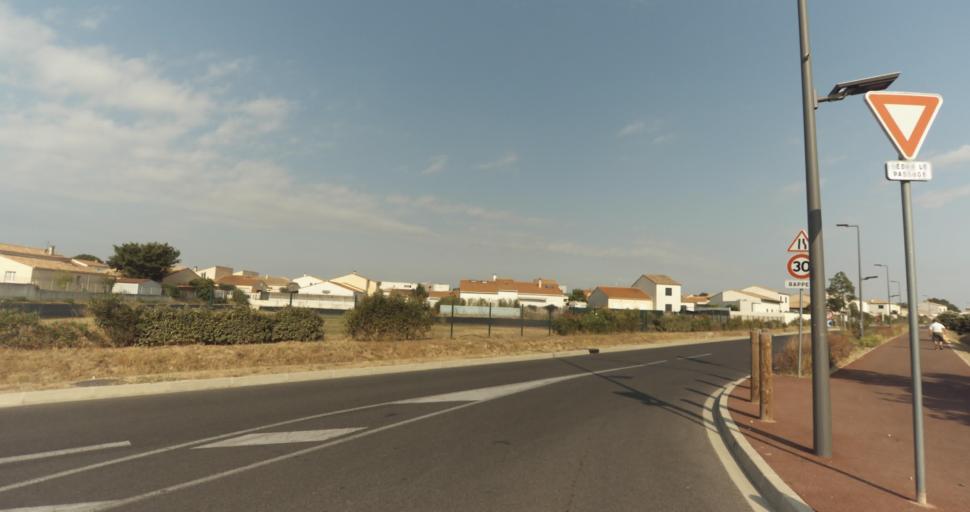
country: FR
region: Languedoc-Roussillon
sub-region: Departement des Pyrenees-Orientales
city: Latour-Bas-Elne
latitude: 42.6090
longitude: 2.9972
